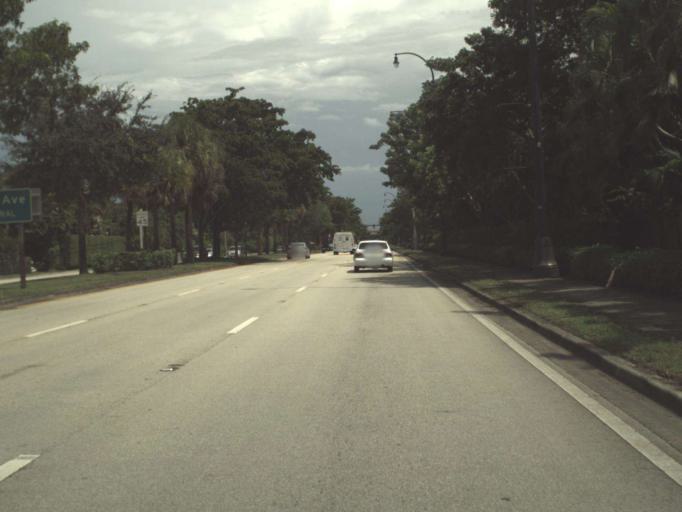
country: US
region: Florida
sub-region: Broward County
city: Plantation
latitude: 26.1208
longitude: -80.2244
